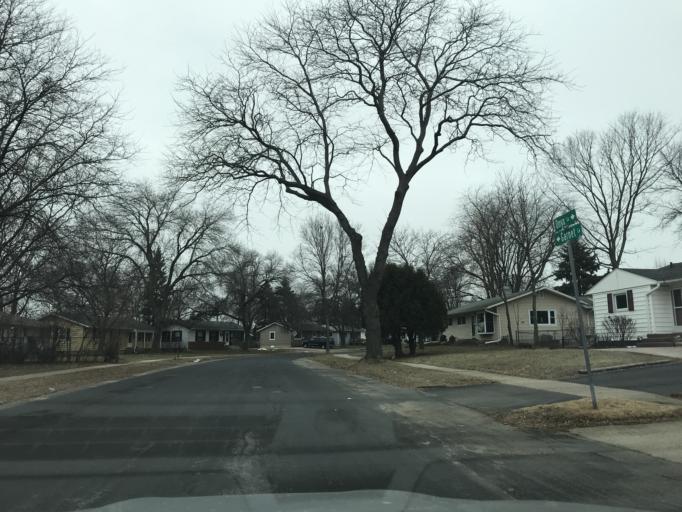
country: US
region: Wisconsin
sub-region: Dane County
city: Monona
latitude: 43.0921
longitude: -89.3054
